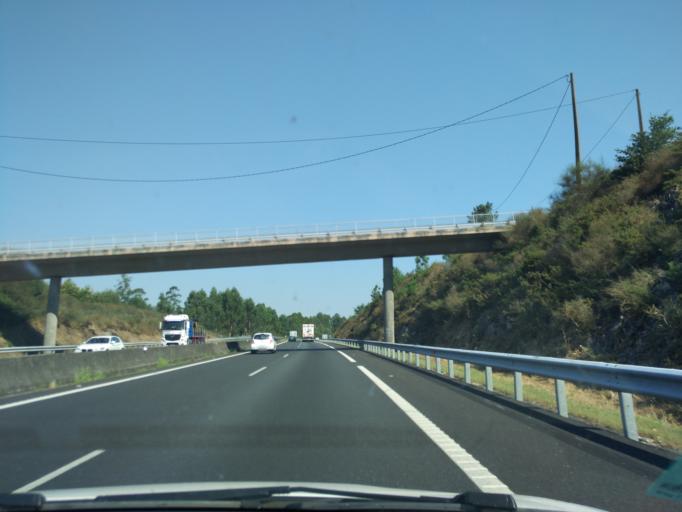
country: ES
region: Galicia
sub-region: Provincia da Coruna
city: Padron
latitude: 42.7496
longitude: -8.6452
